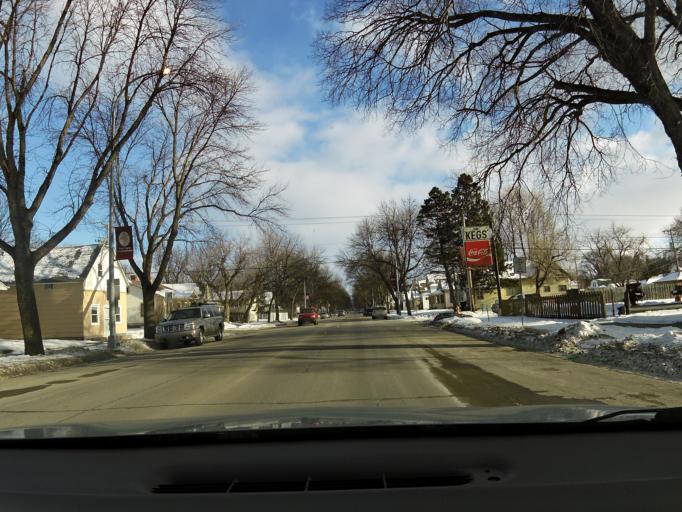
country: US
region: North Dakota
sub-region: Grand Forks County
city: Grand Forks
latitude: 47.9304
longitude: -97.0444
